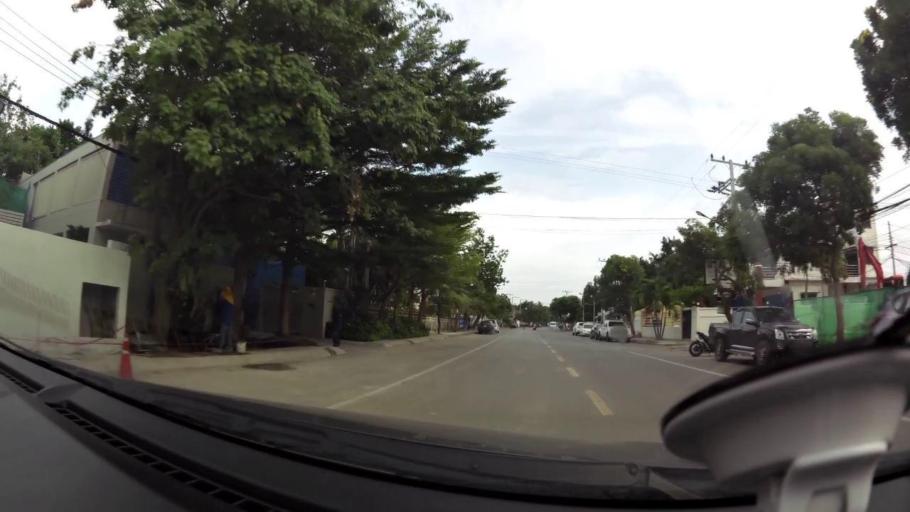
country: TH
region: Prachuap Khiri Khan
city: Hua Hin
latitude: 12.5848
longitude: 99.9552
